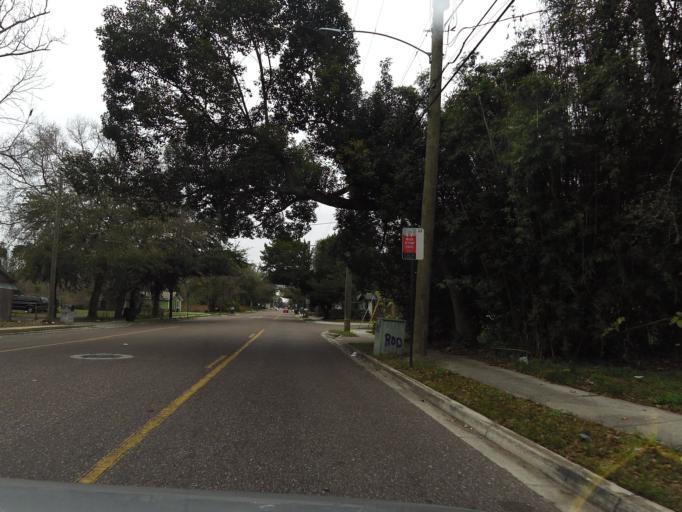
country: US
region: Florida
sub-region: Duval County
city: Jacksonville
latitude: 30.3678
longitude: -81.6989
